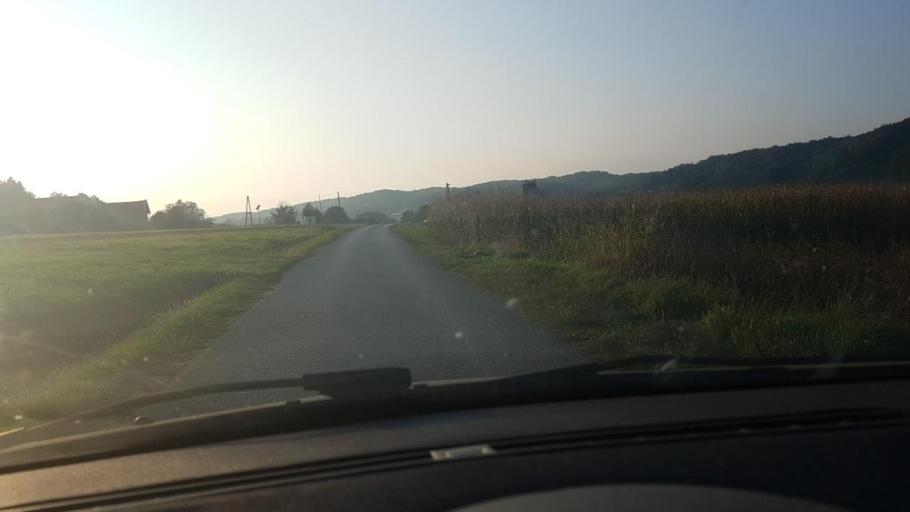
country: SI
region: Majsperk
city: Majsperk
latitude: 46.3349
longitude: 15.7197
